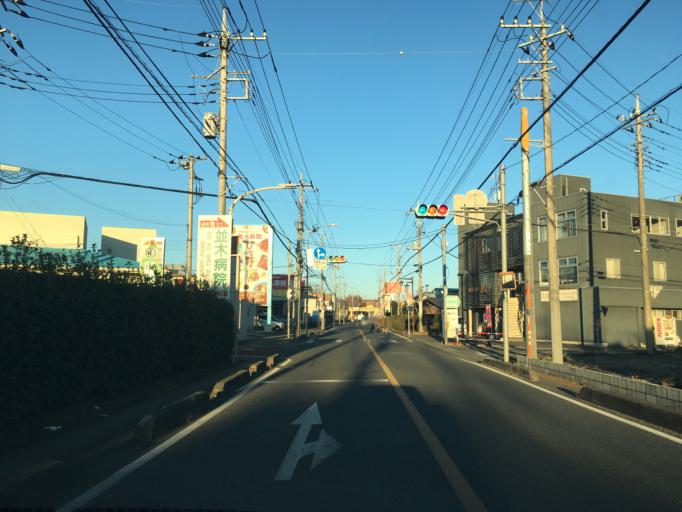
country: JP
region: Saitama
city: Sayama
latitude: 35.8128
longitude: 139.4265
